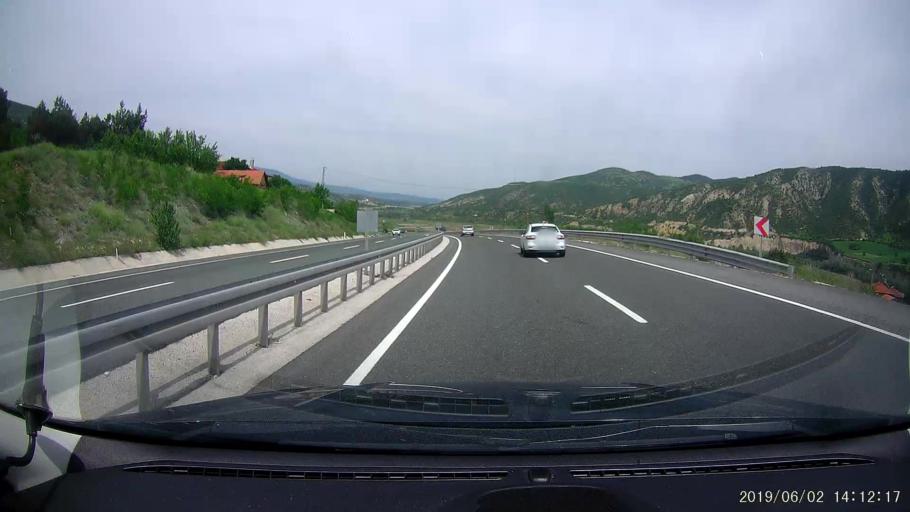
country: TR
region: Cankiri
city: Yaprakli
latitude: 40.9112
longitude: 33.8065
